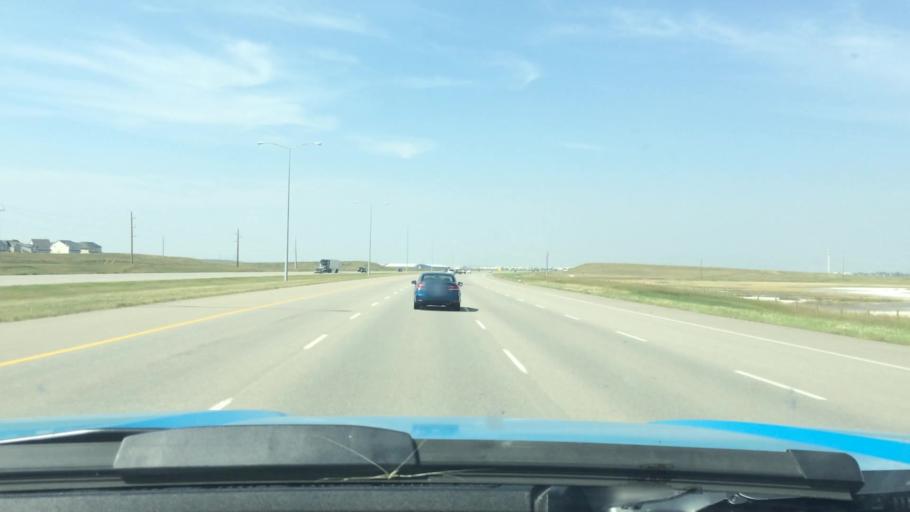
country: CA
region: Alberta
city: Chestermere
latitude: 50.9212
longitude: -113.9154
